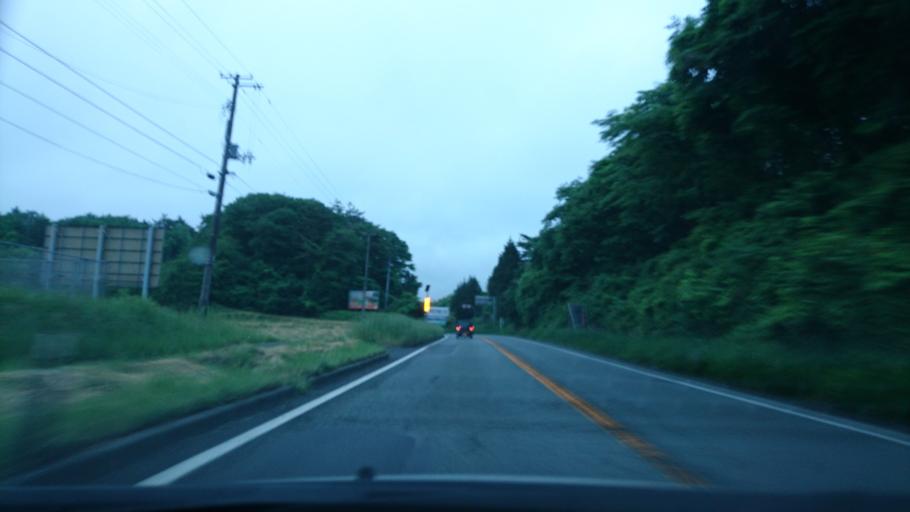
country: JP
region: Iwate
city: Ichinoseki
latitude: 38.8819
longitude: 141.1182
